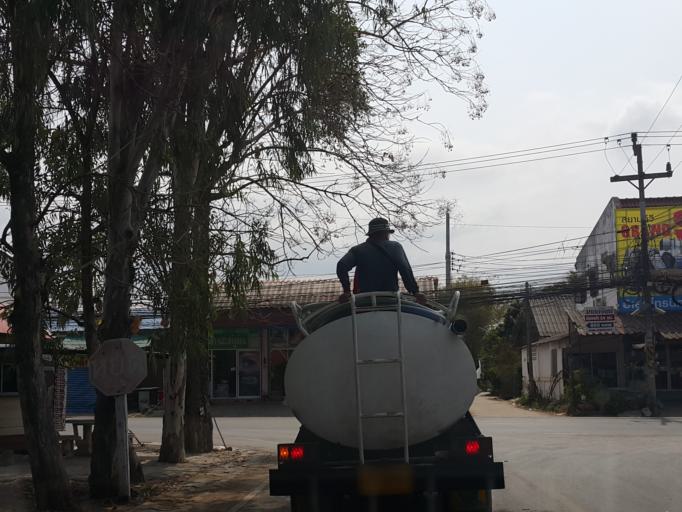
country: TH
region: Lamphun
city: Ban Thi
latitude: 18.6504
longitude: 99.1240
